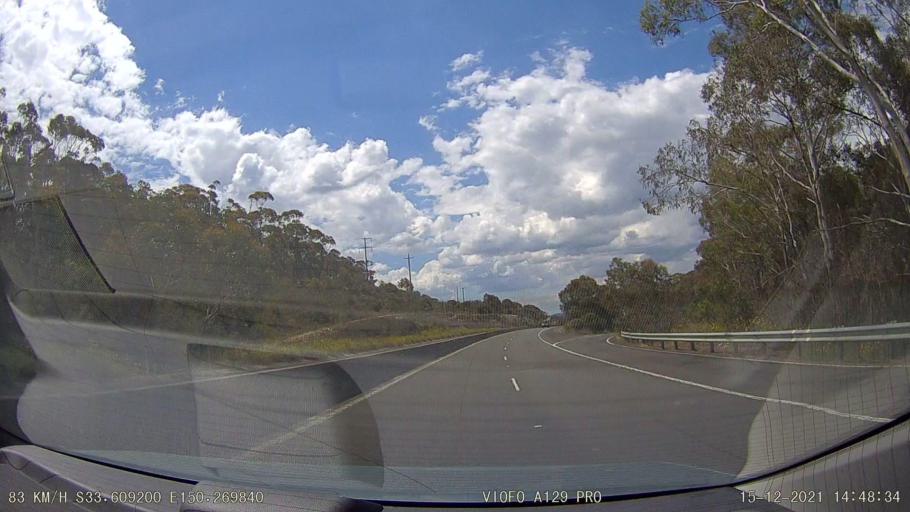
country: AU
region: New South Wales
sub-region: Blue Mountains Municipality
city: Blackheath
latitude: -33.6096
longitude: 150.2699
